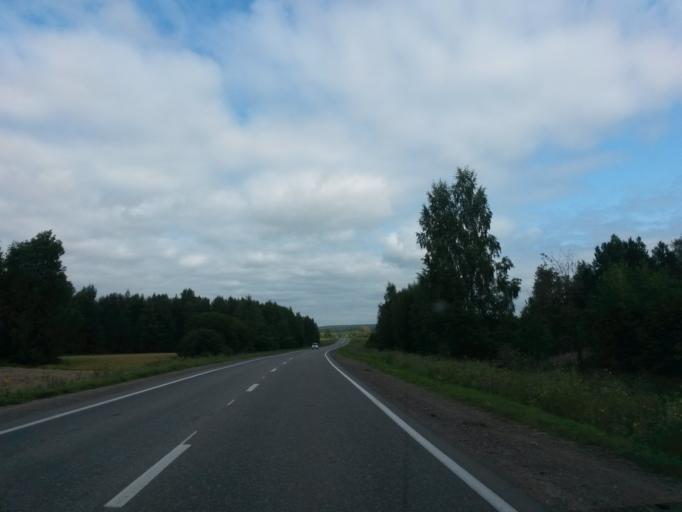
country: RU
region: Jaroslavl
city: Gavrilov-Yam
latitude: 57.3148
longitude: 39.9342
